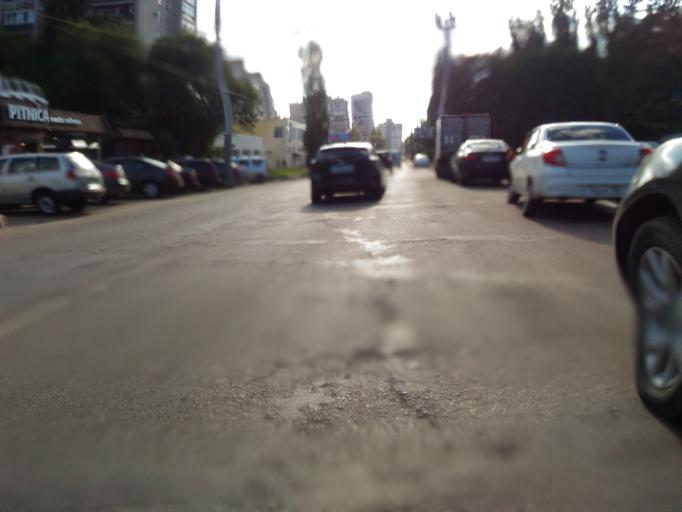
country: RU
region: Voronezj
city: Voronezh
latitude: 51.6517
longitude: 39.1326
